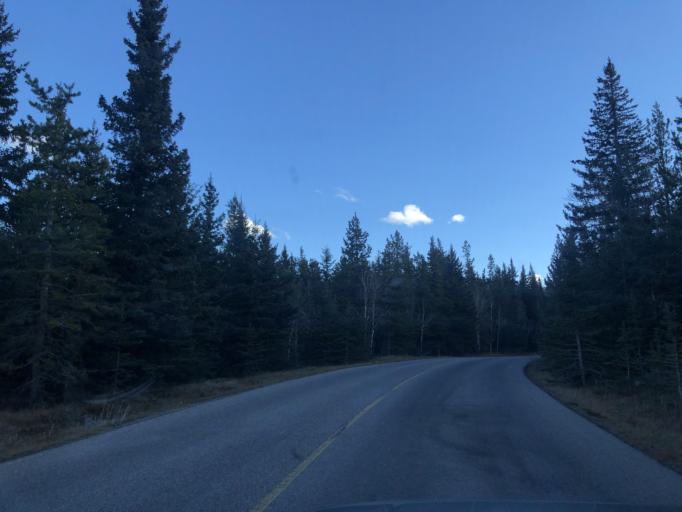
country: CA
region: Alberta
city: Canmore
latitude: 51.0800
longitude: -115.0787
